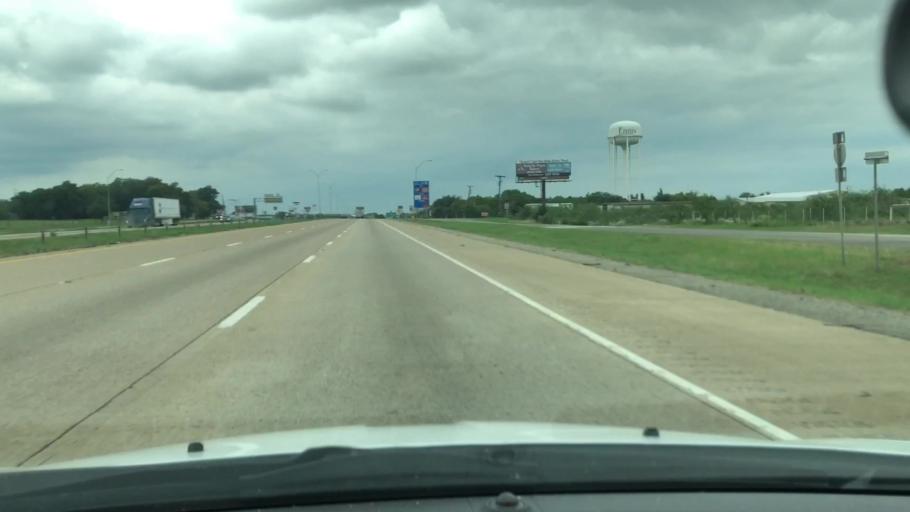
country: US
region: Texas
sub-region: Ellis County
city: Ennis
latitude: 32.3253
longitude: -96.6092
